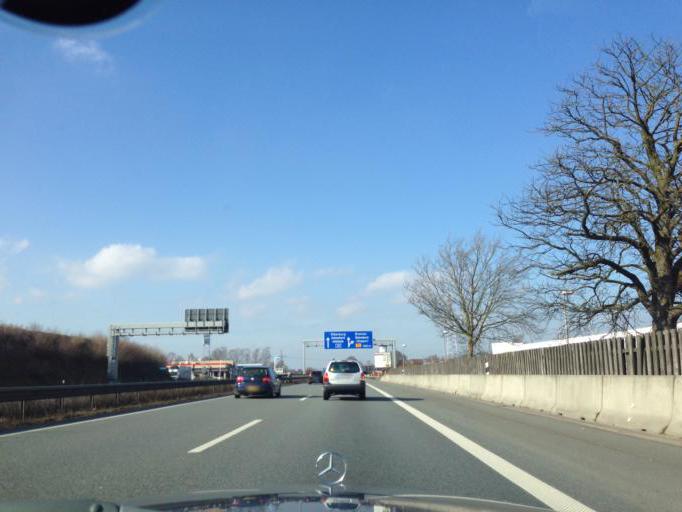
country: DE
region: Lower Saxony
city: Stuhr
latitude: 53.0194
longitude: 8.6909
